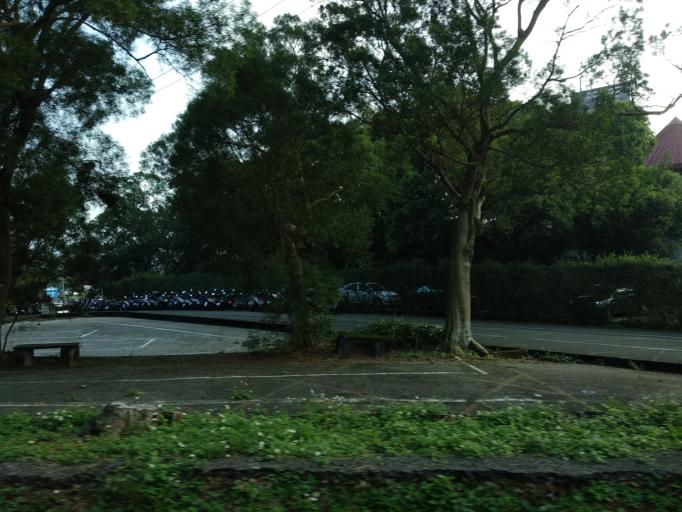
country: TW
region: Taiwan
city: Daxi
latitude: 24.8227
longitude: 121.1845
